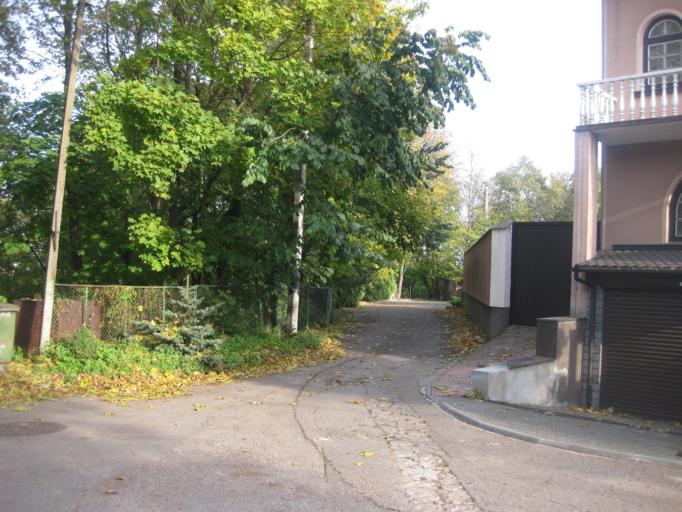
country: LT
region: Kauno apskritis
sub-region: Kaunas
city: Kaunas
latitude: 54.8937
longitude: 23.8757
